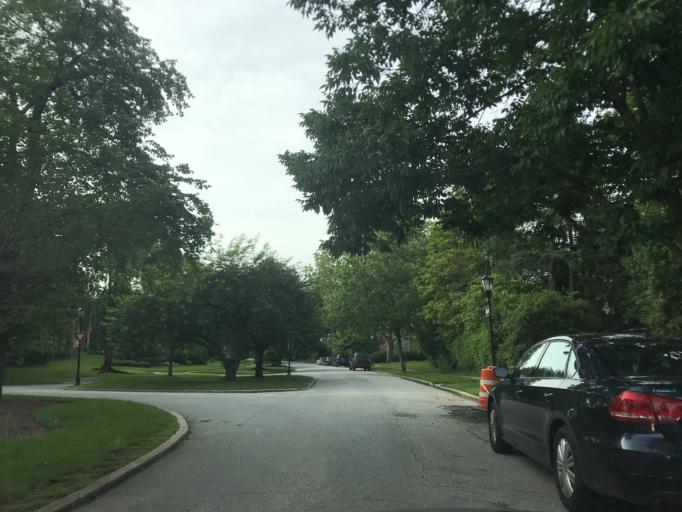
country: US
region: Maryland
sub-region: Baltimore County
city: Towson
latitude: 39.3589
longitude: -76.6158
